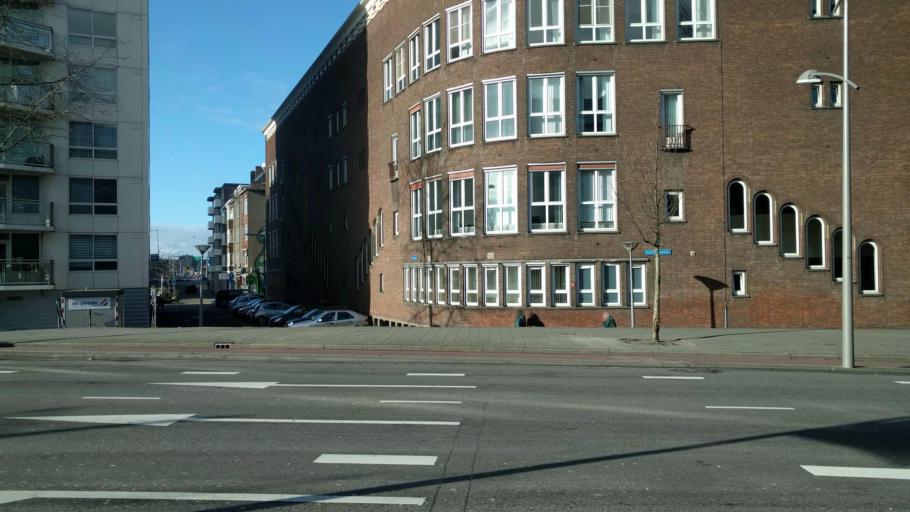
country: NL
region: South Holland
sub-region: Gemeente Rotterdam
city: Rotterdam
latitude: 51.9156
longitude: 4.4815
